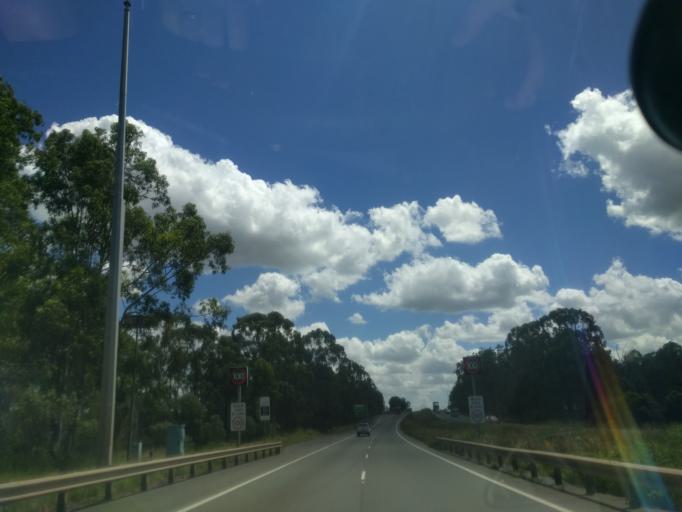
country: AU
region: Queensland
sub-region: Ipswich
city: Riverview
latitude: -27.6039
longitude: 152.8310
